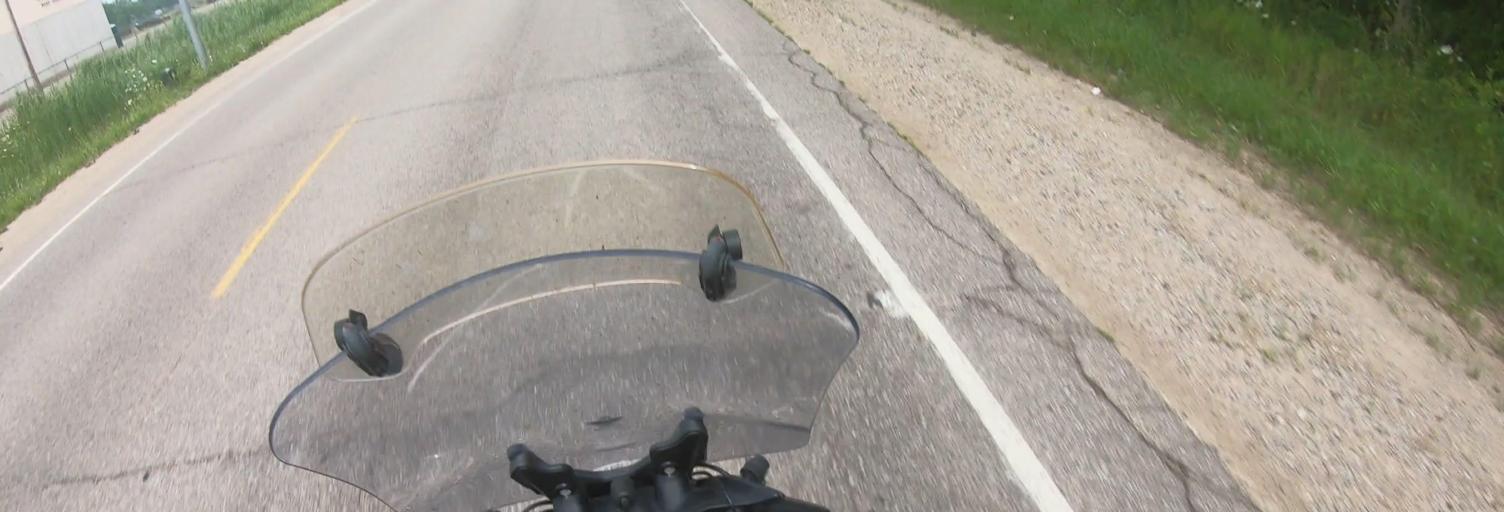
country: US
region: Michigan
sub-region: Shiawassee County
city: Perry
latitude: 42.8409
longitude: -84.1997
